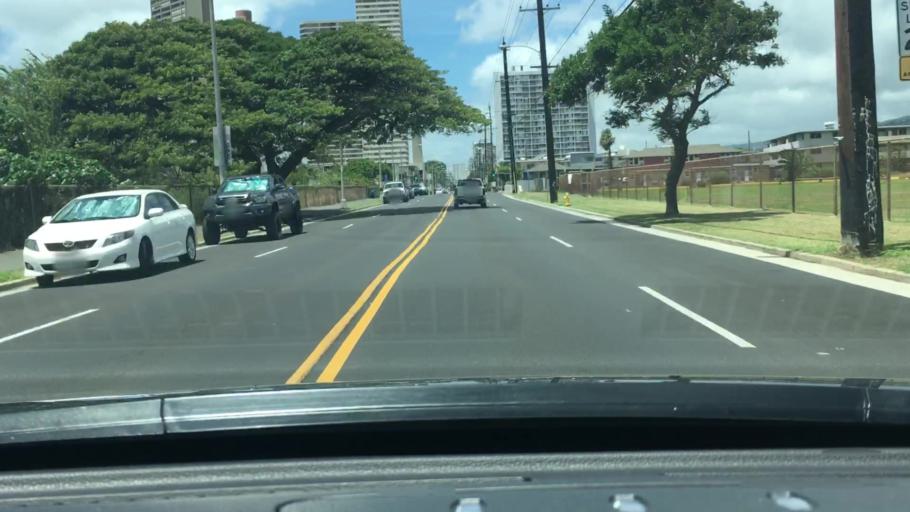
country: US
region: Hawaii
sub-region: Honolulu County
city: Honolulu
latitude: 21.2840
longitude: -157.8196
